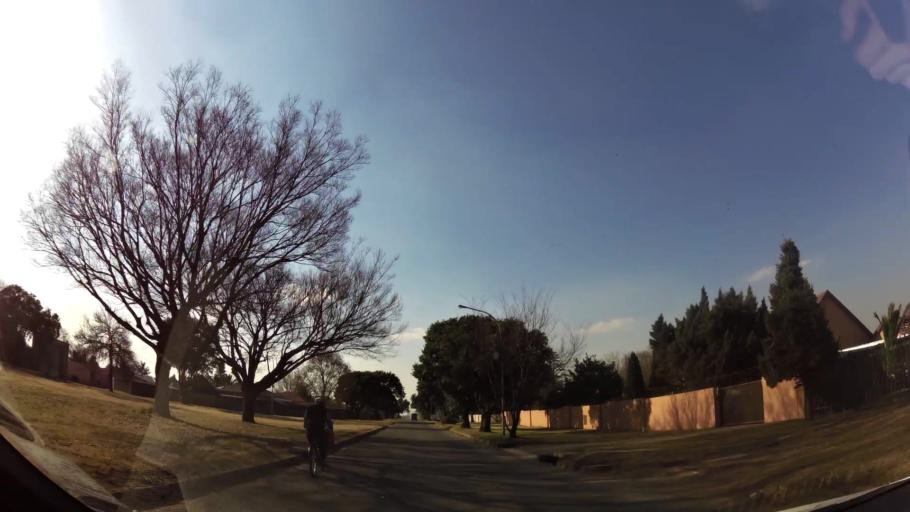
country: ZA
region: Gauteng
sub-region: Ekurhuleni Metropolitan Municipality
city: Brakpan
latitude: -26.2222
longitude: 28.3615
